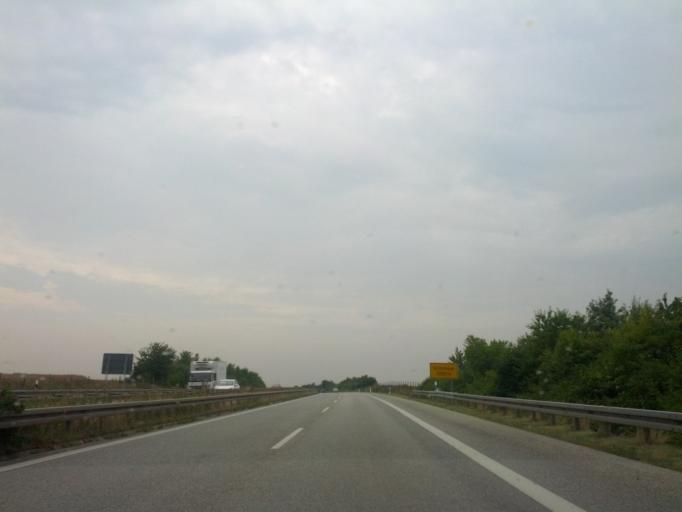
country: DE
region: Mecklenburg-Vorpommern
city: Kritzmow
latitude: 54.0572
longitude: 12.0396
